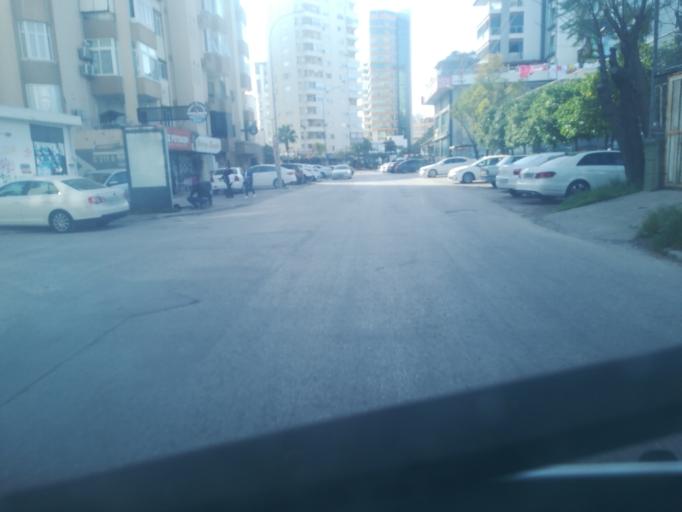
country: TR
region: Adana
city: Adana
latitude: 37.0410
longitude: 35.3153
